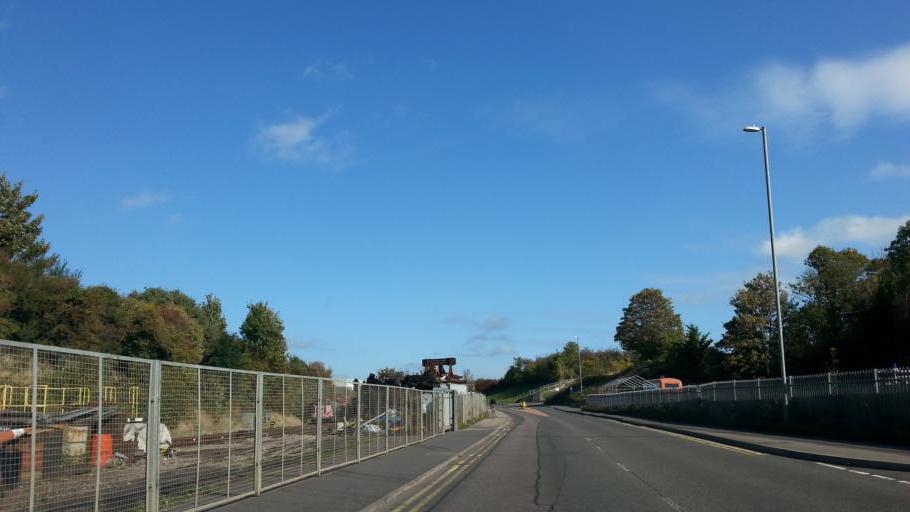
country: GB
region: England
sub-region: Northamptonshire
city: Rushden
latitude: 52.2949
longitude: -0.5963
